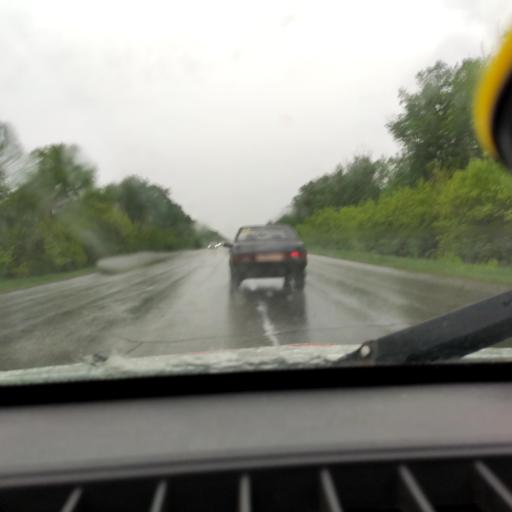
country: RU
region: Samara
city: Tol'yatti
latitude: 53.6155
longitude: 49.4131
